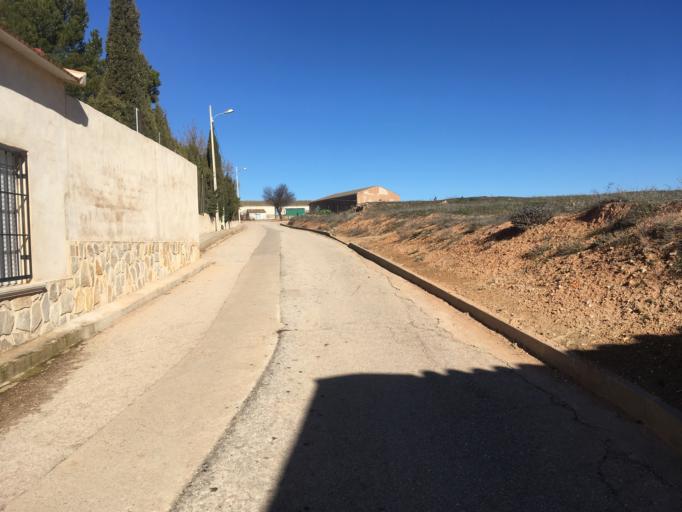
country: ES
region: Castille-La Mancha
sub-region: Provincia de Cuenca
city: Atalaya del Canavate
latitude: 39.5486
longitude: -2.2475
